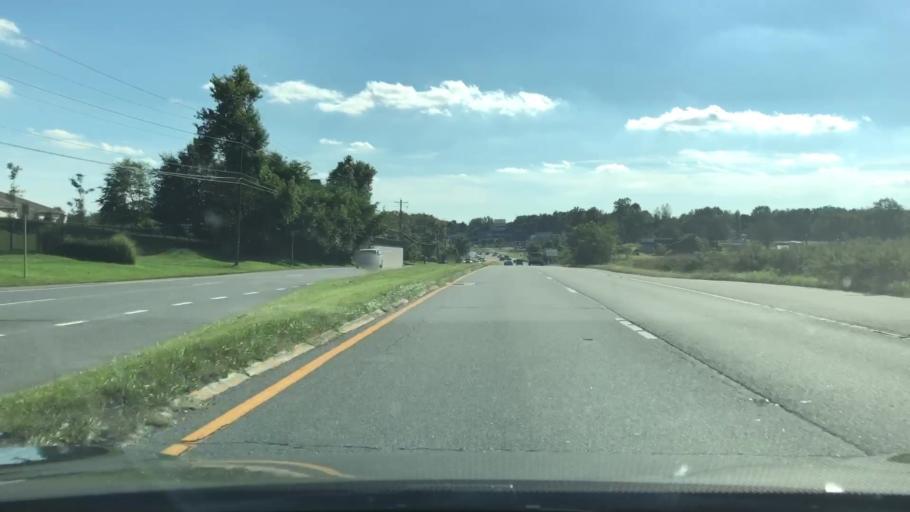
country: US
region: Delaware
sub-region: New Castle County
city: Bellefonte
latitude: 39.8385
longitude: -75.5400
